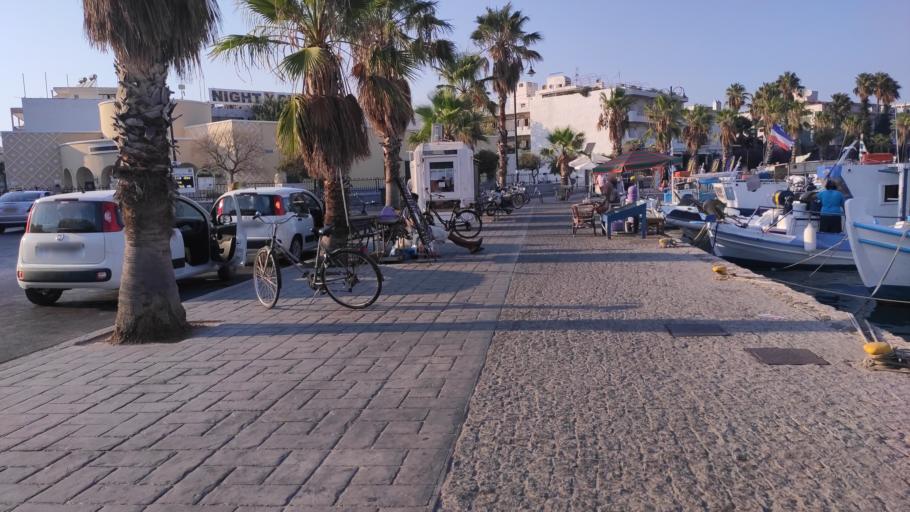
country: GR
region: South Aegean
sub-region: Nomos Dodekanisou
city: Kos
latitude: 36.8958
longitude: 27.2863
